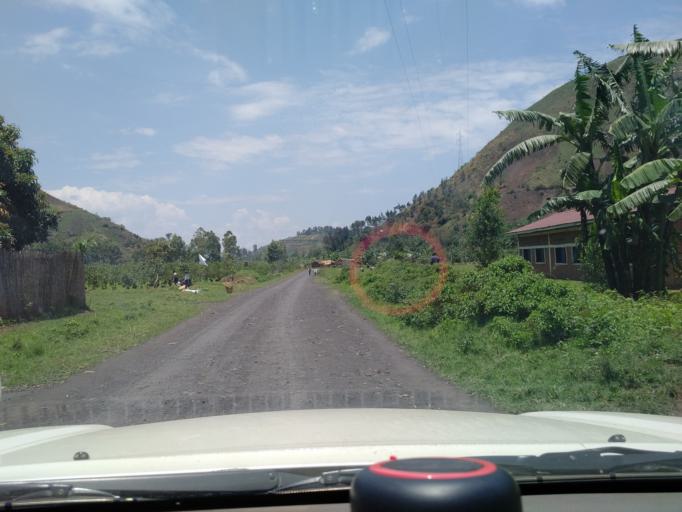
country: CD
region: Nord Kivu
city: Sake
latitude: -1.7670
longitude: 28.9986
